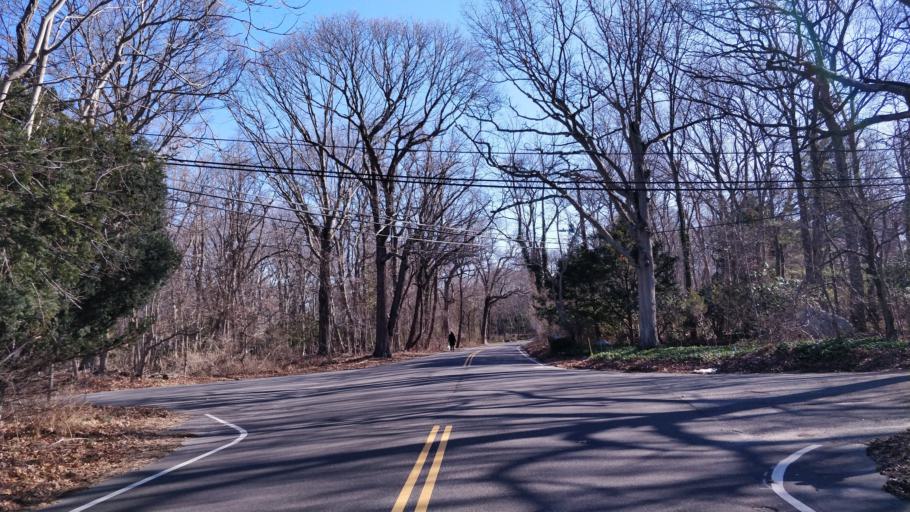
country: US
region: New York
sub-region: Suffolk County
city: Port Jefferson
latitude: 40.9647
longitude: -73.0676
